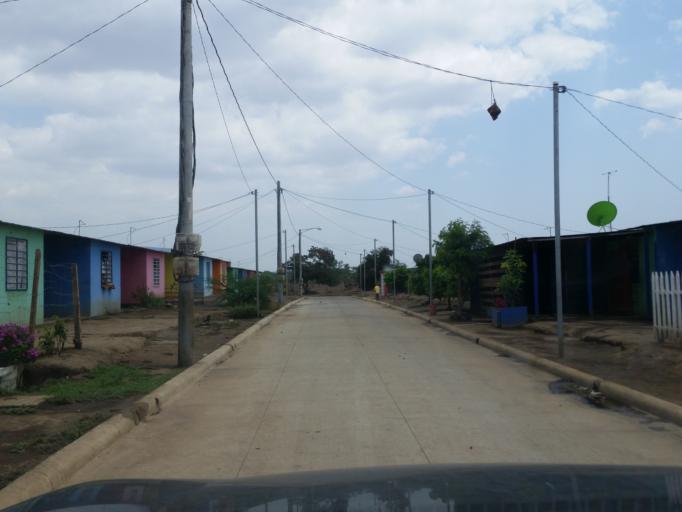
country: NI
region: Managua
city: Managua
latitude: 12.1263
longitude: -86.1584
